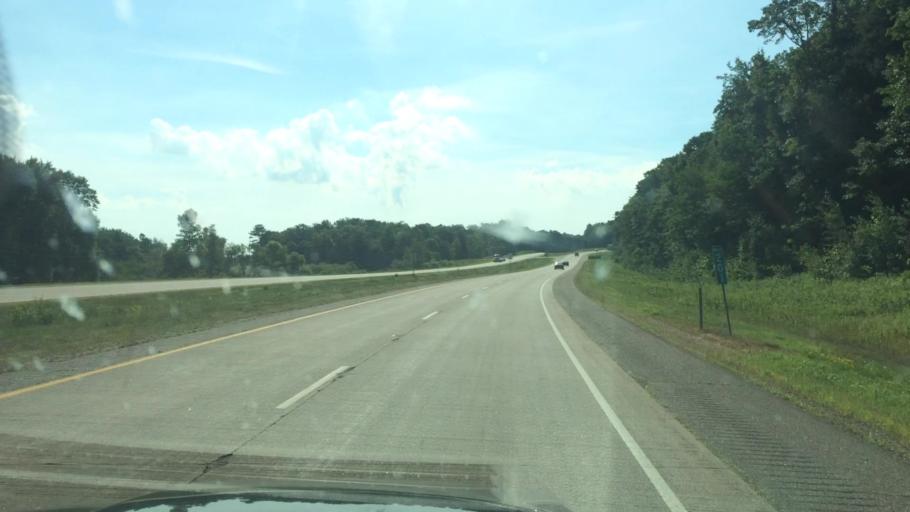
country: US
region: Wisconsin
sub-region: Shawano County
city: Wittenberg
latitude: 44.8254
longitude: -89.0681
